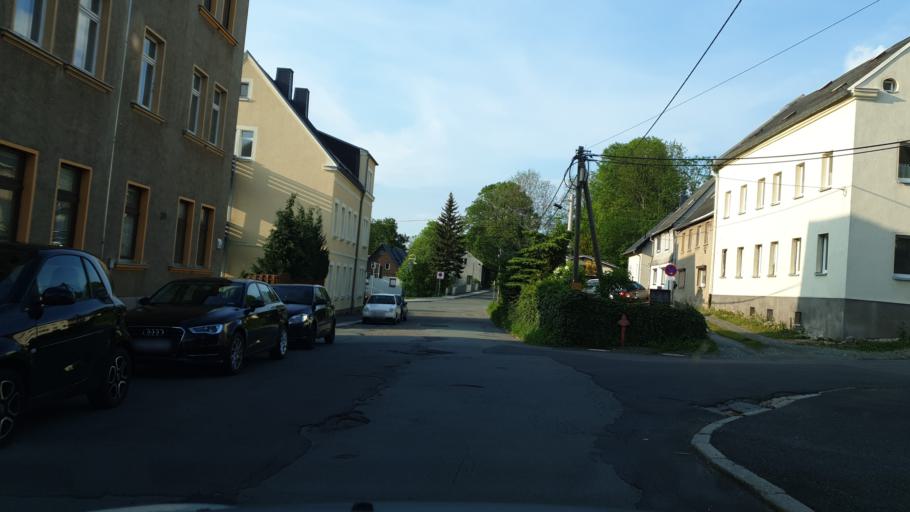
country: DE
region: Saxony
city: Stollberg
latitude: 50.7132
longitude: 12.7863
